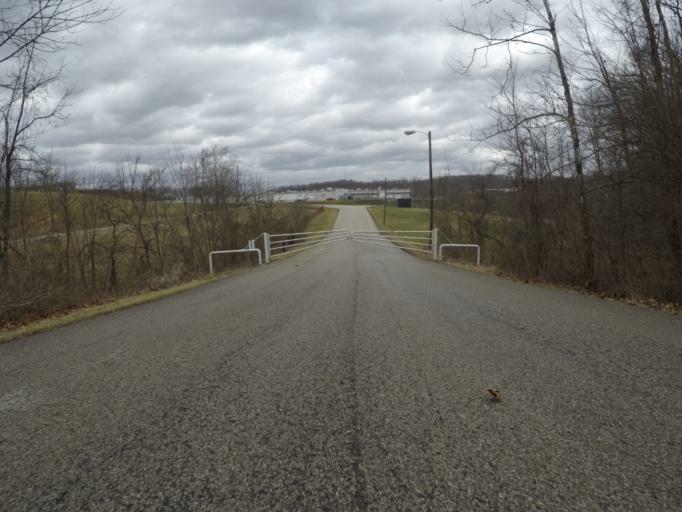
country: US
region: West Virginia
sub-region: Cabell County
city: Pea Ridge
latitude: 38.4047
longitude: -82.3739
